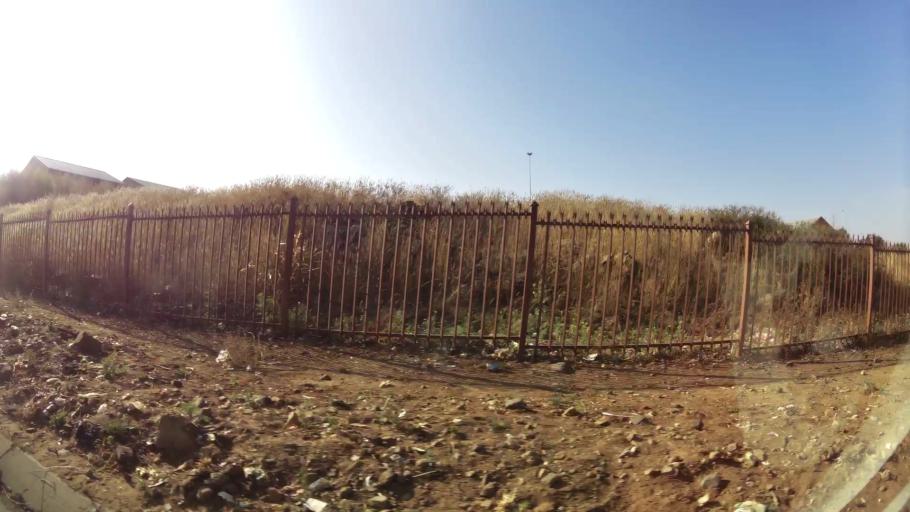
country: ZA
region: Orange Free State
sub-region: Mangaung Metropolitan Municipality
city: Bloemfontein
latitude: -29.1777
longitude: 26.2250
